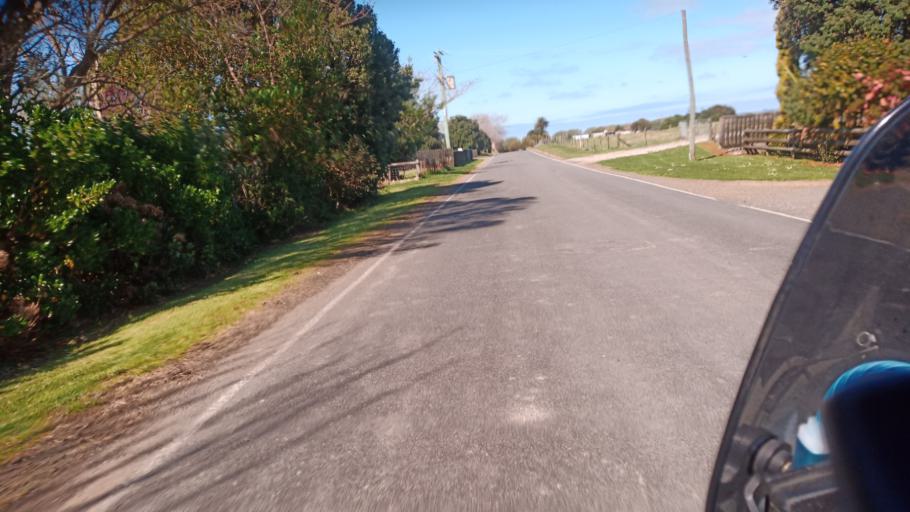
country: NZ
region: Gisborne
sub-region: Gisborne District
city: Gisborne
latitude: -39.0509
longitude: 177.8749
